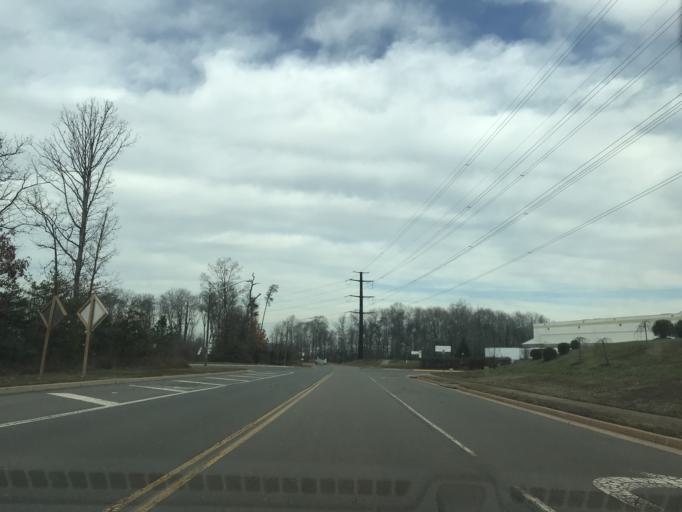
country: US
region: Virginia
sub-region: City of Manassas
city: Manassas
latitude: 38.7242
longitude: -77.5020
